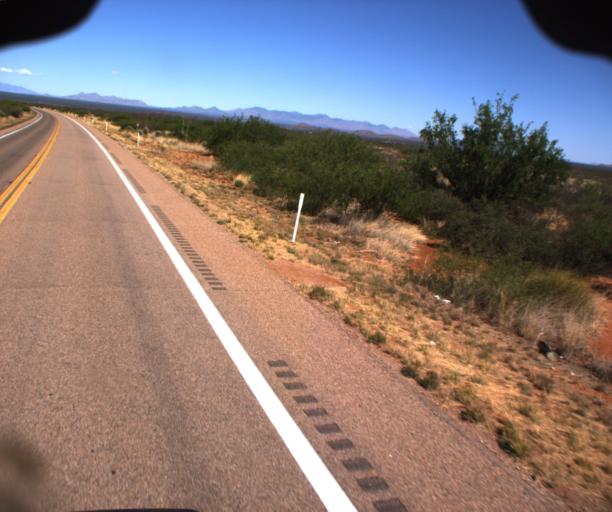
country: US
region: Arizona
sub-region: Cochise County
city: Sierra Vista Southeast
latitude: 31.5415
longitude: -110.0763
